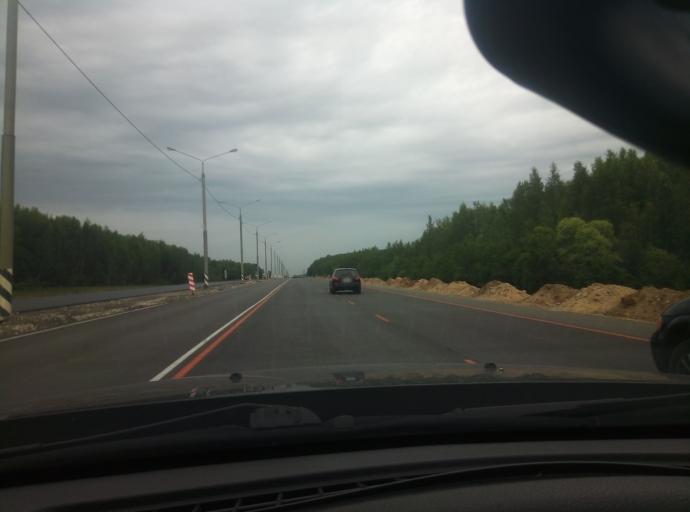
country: RU
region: Tula
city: Yasnogorsk
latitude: 54.5446
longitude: 37.5178
